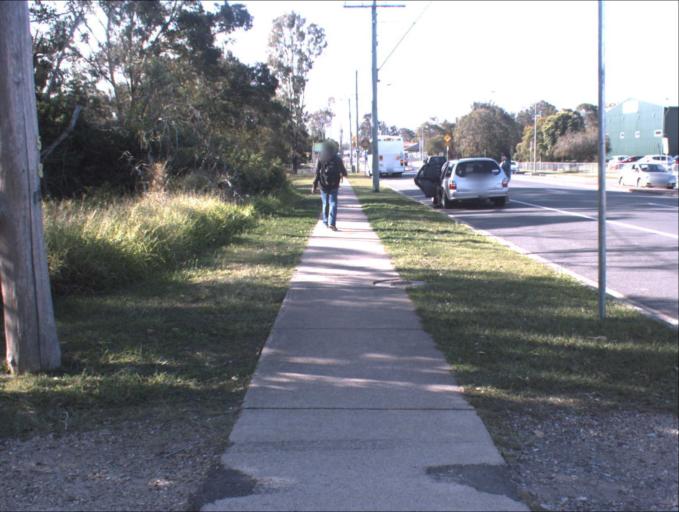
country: AU
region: Queensland
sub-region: Logan
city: Logan City
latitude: -27.6760
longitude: 153.0895
